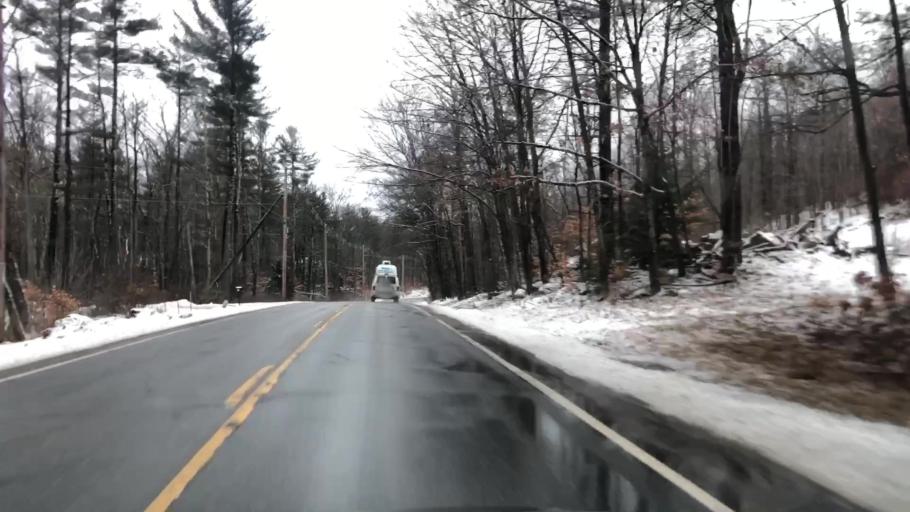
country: US
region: New Hampshire
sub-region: Hillsborough County
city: New Boston
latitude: 43.0158
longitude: -71.6882
